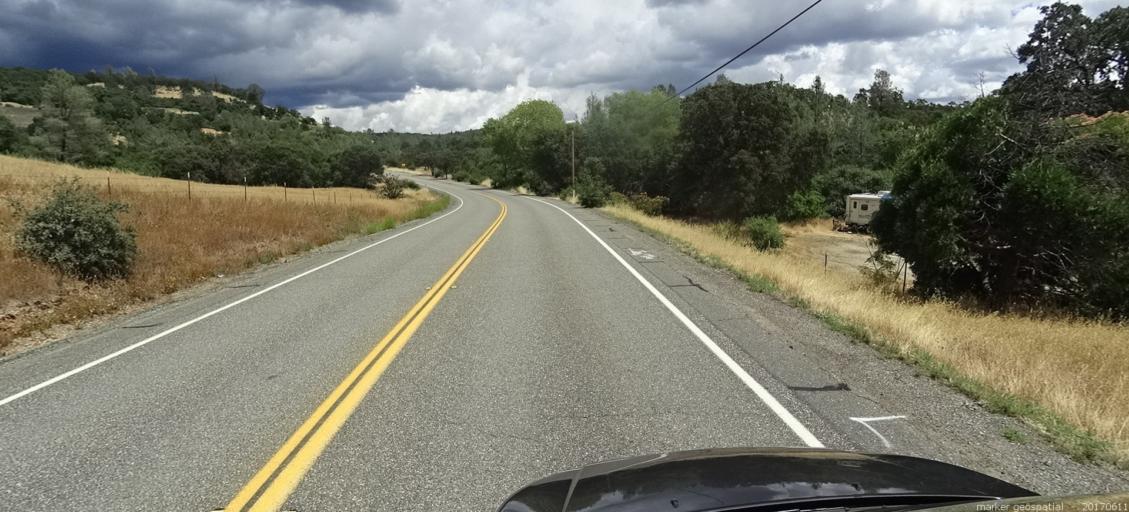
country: US
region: California
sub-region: Butte County
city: Paradise
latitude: 39.6555
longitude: -121.5692
